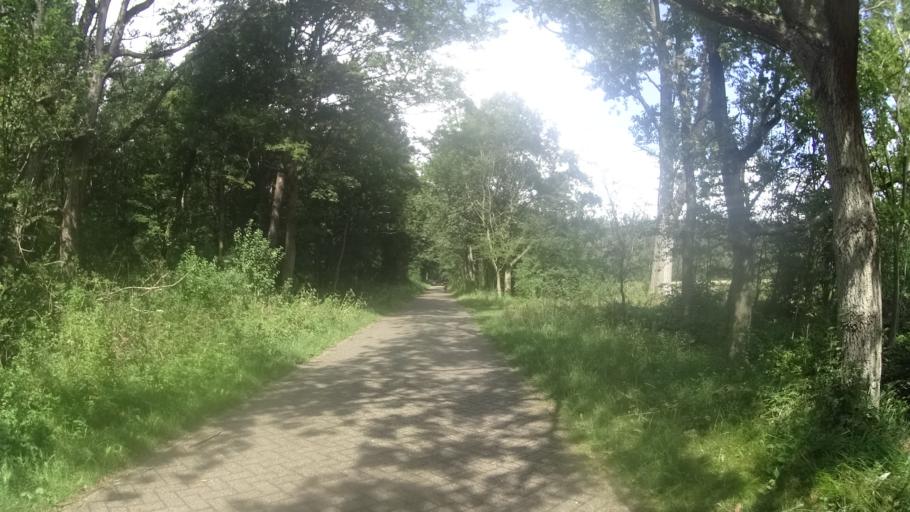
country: NL
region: North Holland
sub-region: Gemeente Castricum
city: Castricum
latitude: 52.5653
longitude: 4.6394
